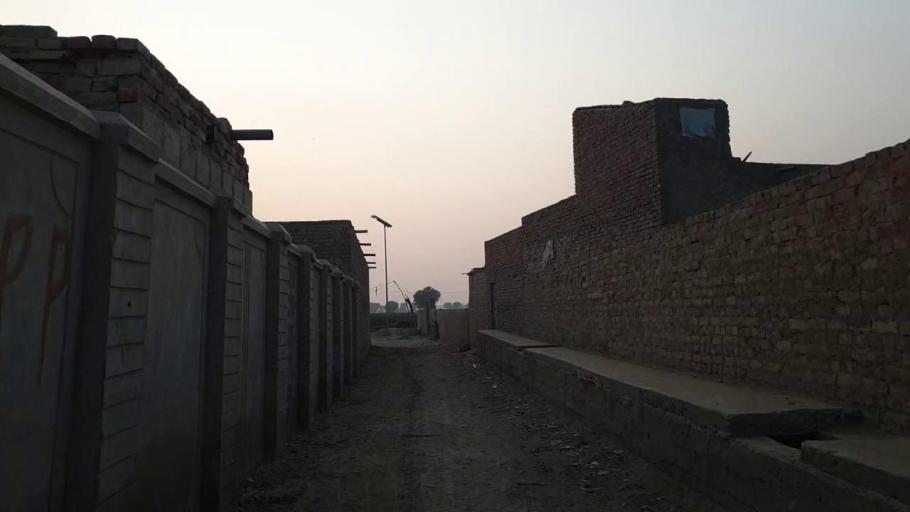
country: PK
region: Sindh
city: Bhan
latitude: 26.5259
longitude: 67.7098
